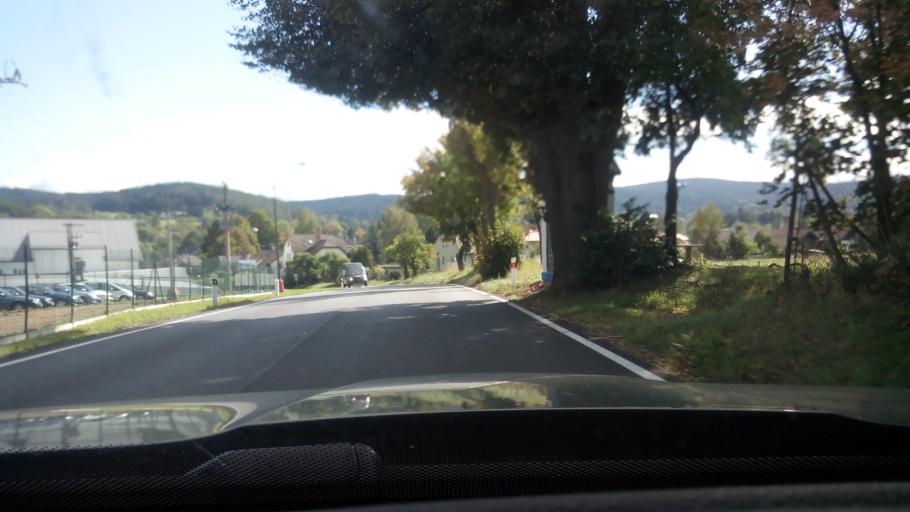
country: CZ
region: Jihocesky
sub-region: Okres Prachatice
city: Zdikov
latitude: 49.0877
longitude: 13.6931
